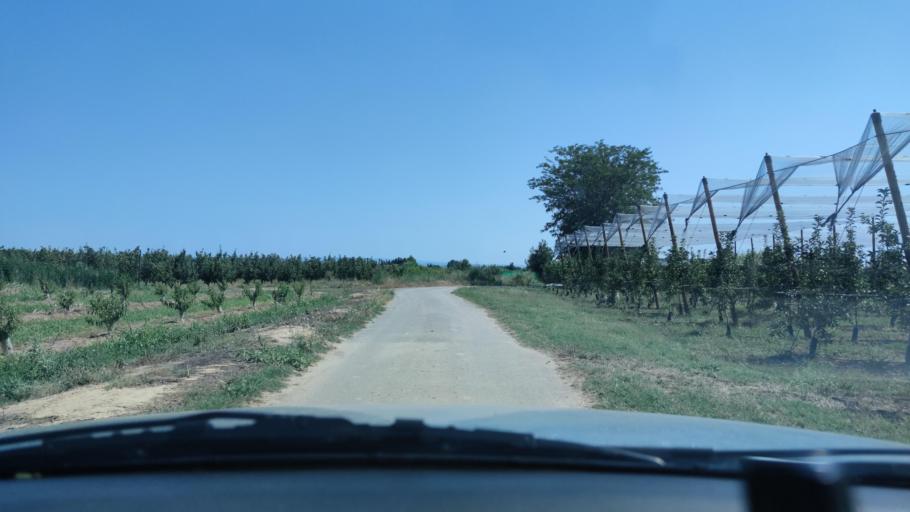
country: ES
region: Catalonia
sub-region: Provincia de Lleida
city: Corbins
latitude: 41.6762
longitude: 0.6609
